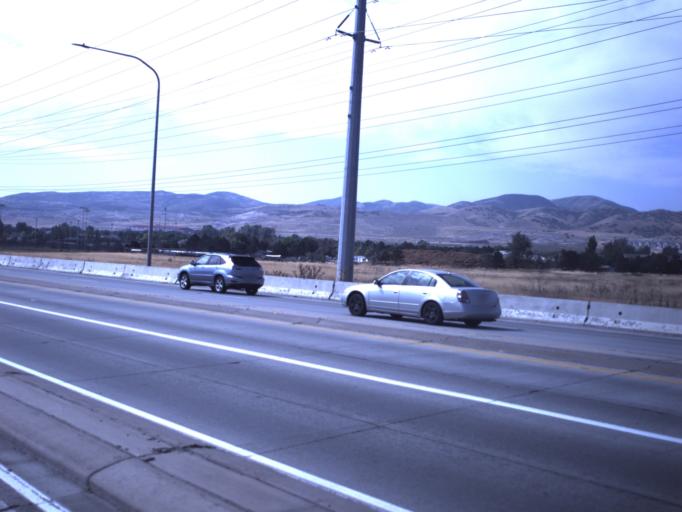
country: US
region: Utah
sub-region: Salt Lake County
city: Riverton
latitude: 40.5071
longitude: -111.9822
